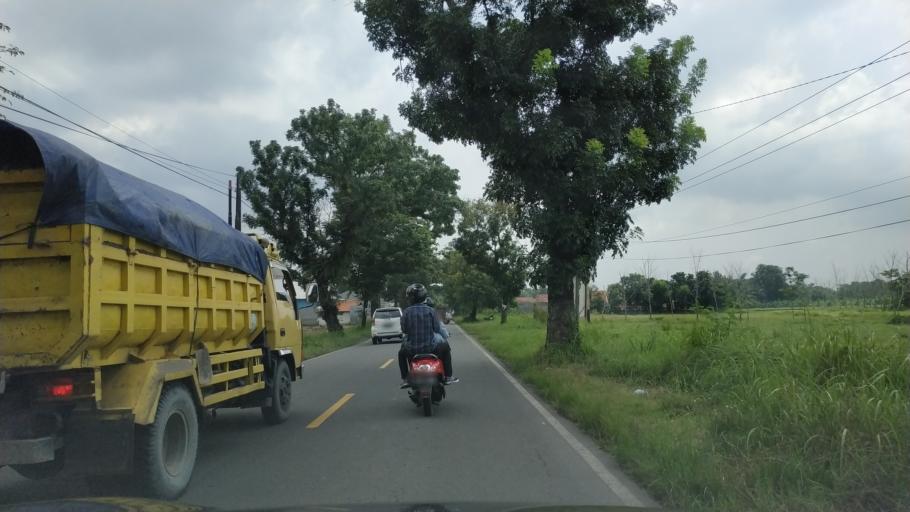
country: ID
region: Central Java
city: Lebaksiu
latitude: -7.0261
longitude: 109.1428
